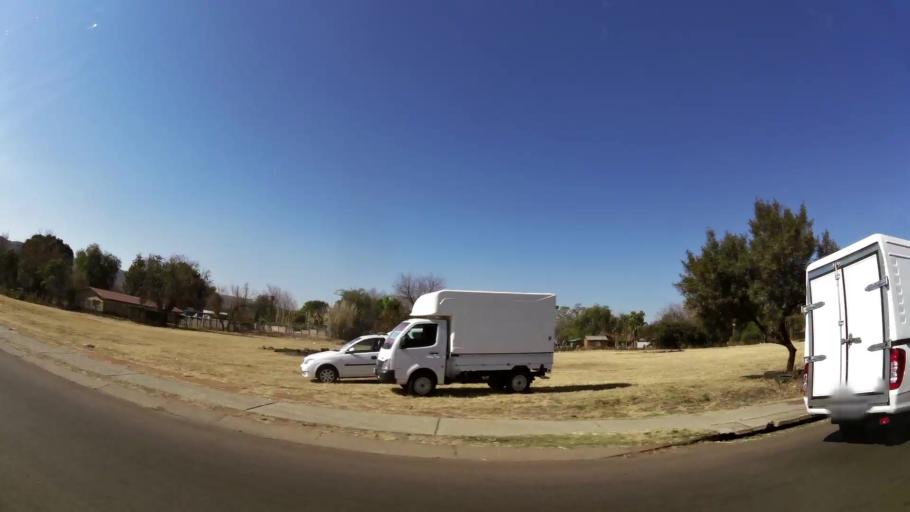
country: ZA
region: Gauteng
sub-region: City of Tshwane Metropolitan Municipality
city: Pretoria
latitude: -25.7102
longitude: 28.2028
